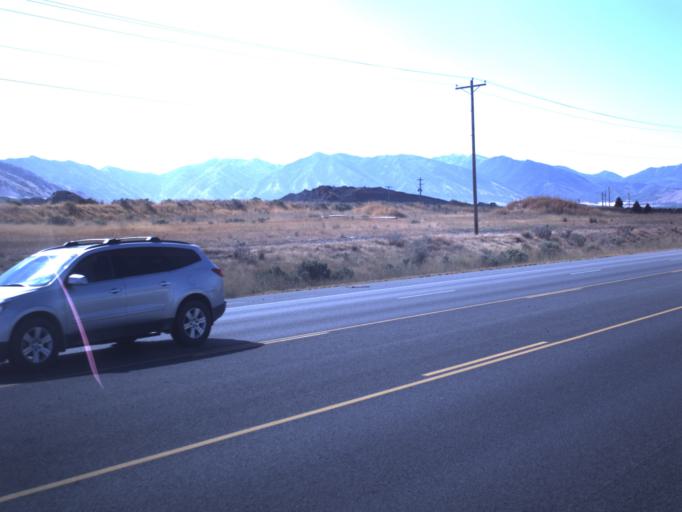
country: US
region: Utah
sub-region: Tooele County
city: Stansbury park
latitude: 40.6335
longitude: -112.2901
